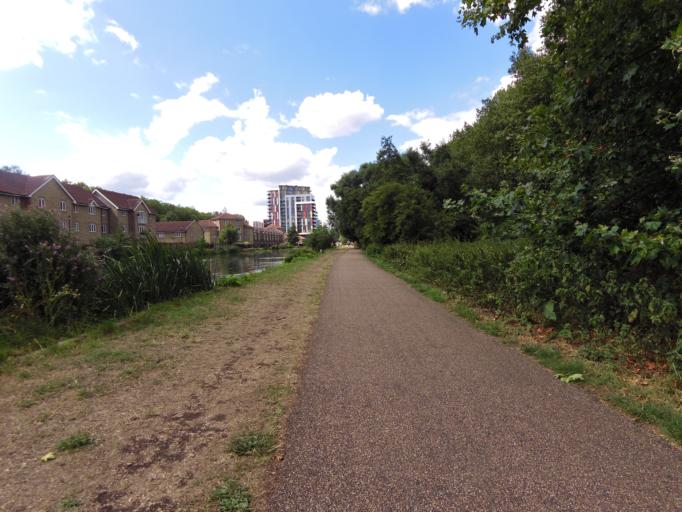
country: GB
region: England
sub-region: Greater London
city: Hackney
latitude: 51.5497
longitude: -0.0280
